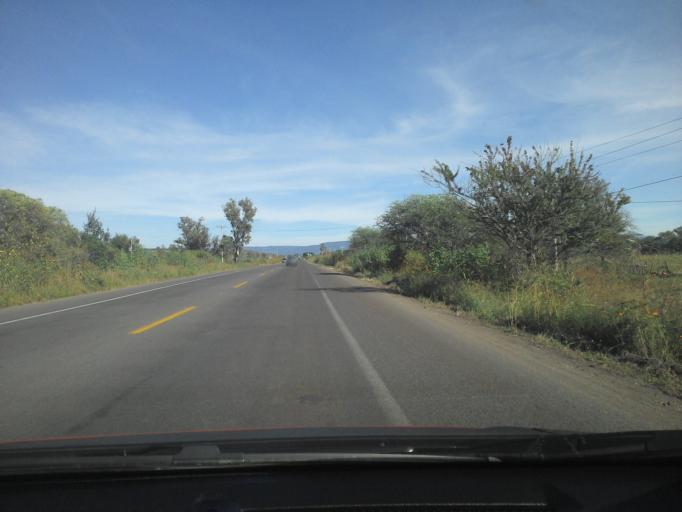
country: MX
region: Jalisco
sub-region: Teuchitlan
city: La Estanzuela
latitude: 20.6723
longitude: -103.8189
